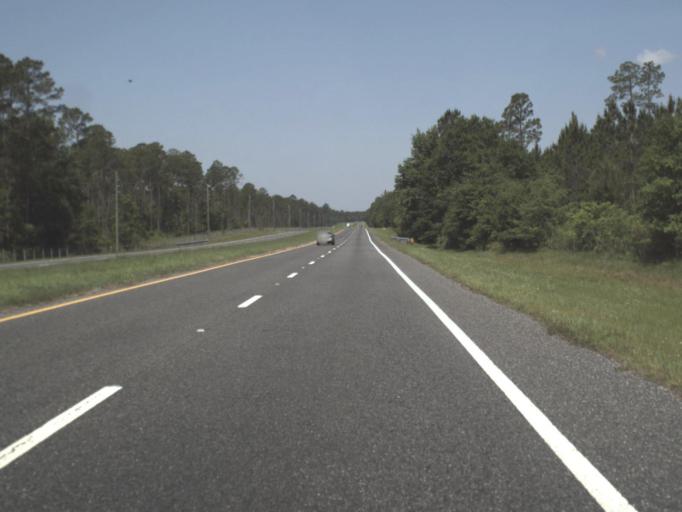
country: US
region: Florida
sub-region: Clay County
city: Middleburg
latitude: 29.9785
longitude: -81.9071
